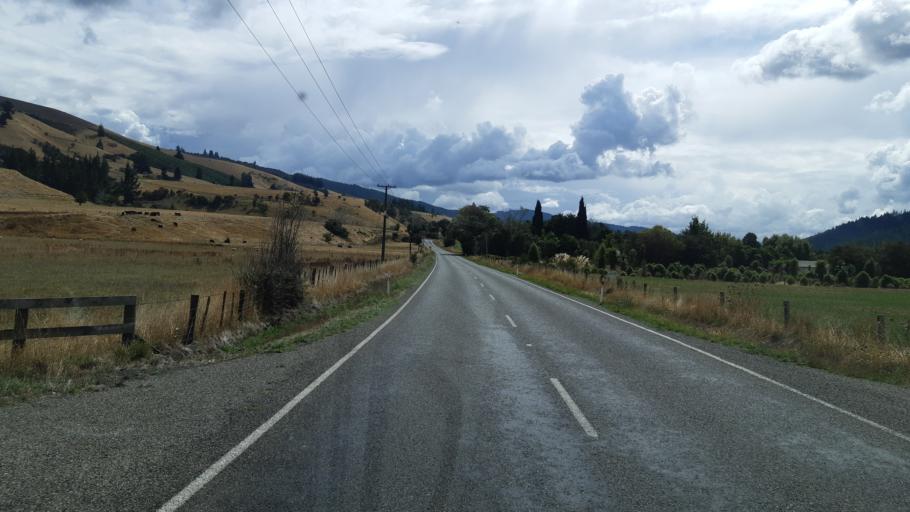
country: NZ
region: Tasman
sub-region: Tasman District
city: Wakefield
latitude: -41.5116
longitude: 172.7954
